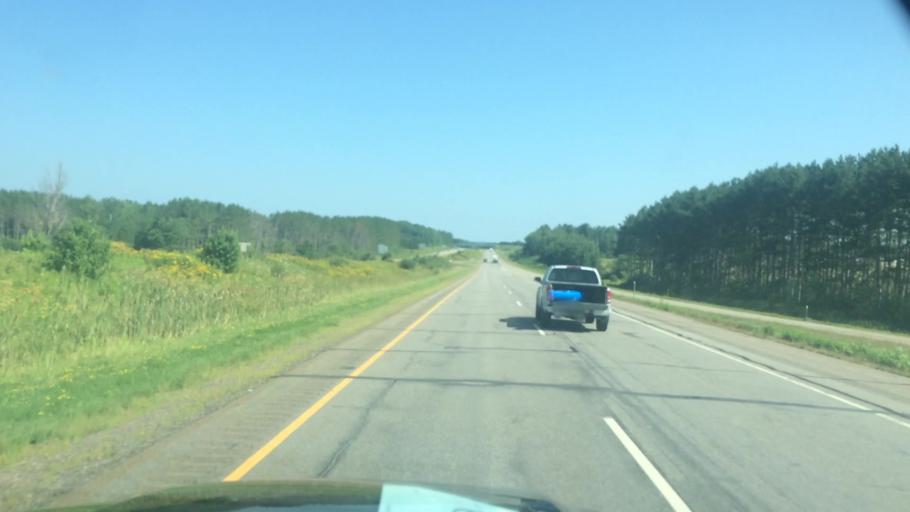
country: US
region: Wisconsin
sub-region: Lincoln County
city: Merrill
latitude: 45.1798
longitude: -89.6464
